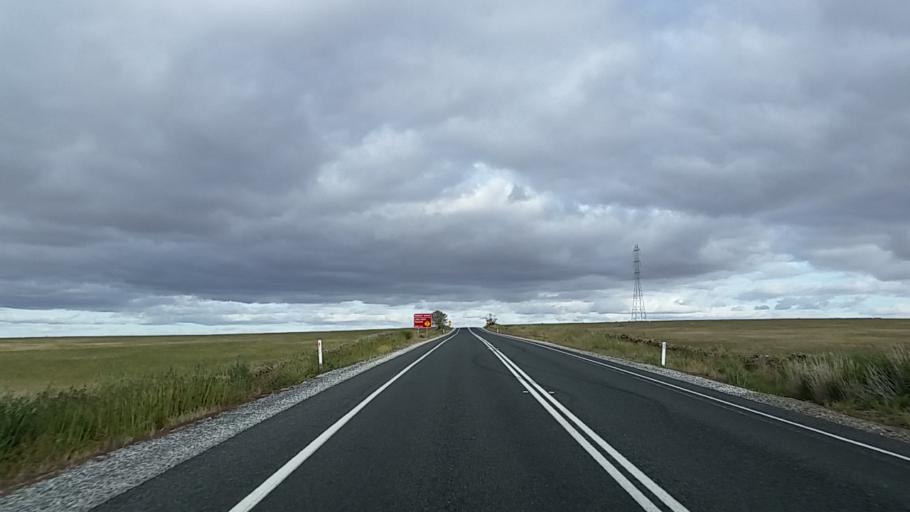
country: AU
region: South Australia
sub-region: Barossa
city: Angaston
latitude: -34.5613
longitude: 139.1933
